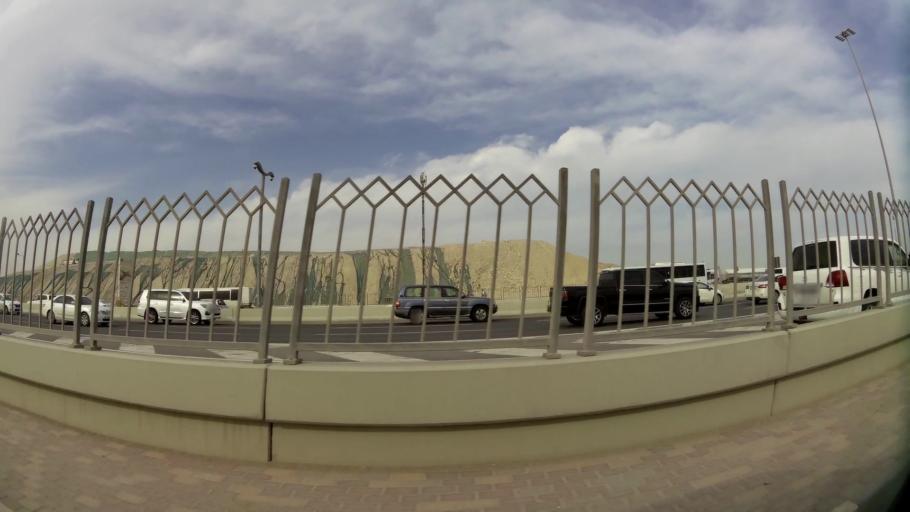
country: QA
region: Baladiyat ad Dawhah
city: Doha
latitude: 25.2880
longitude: 51.4800
